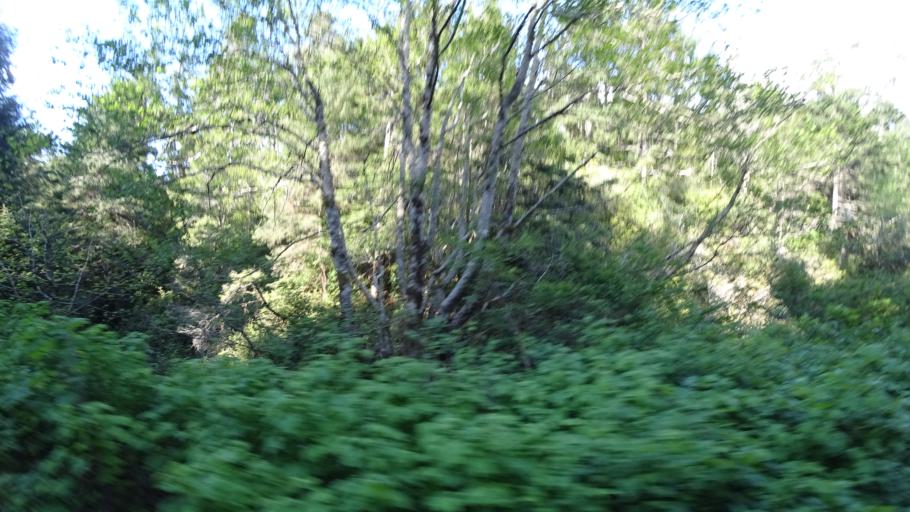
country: US
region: Oregon
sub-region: Douglas County
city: Reedsport
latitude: 43.7478
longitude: -124.1752
